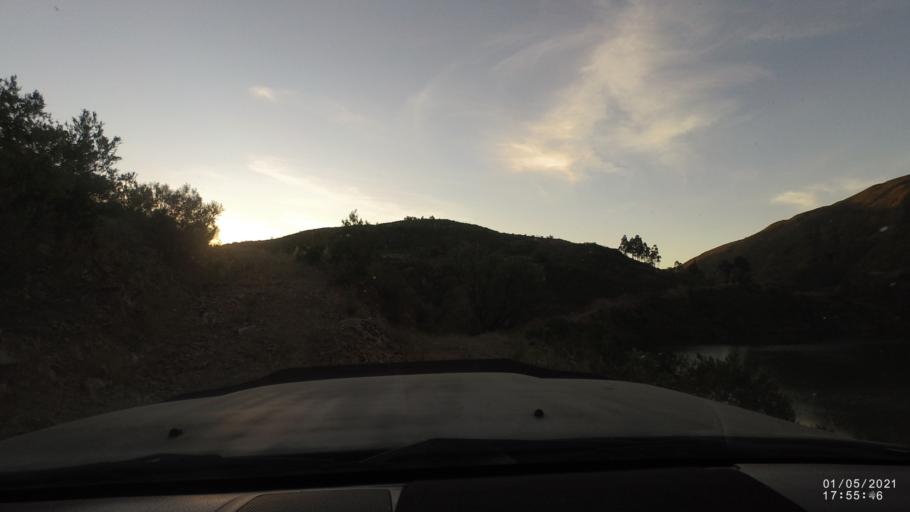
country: BO
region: Cochabamba
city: Capinota
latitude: -17.6863
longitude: -66.1563
